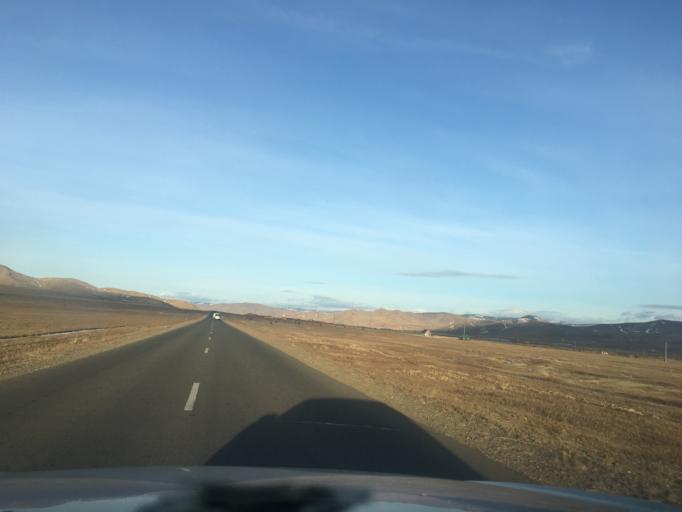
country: MN
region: Central Aimak
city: Mandal
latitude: 48.0945
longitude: 106.6097
